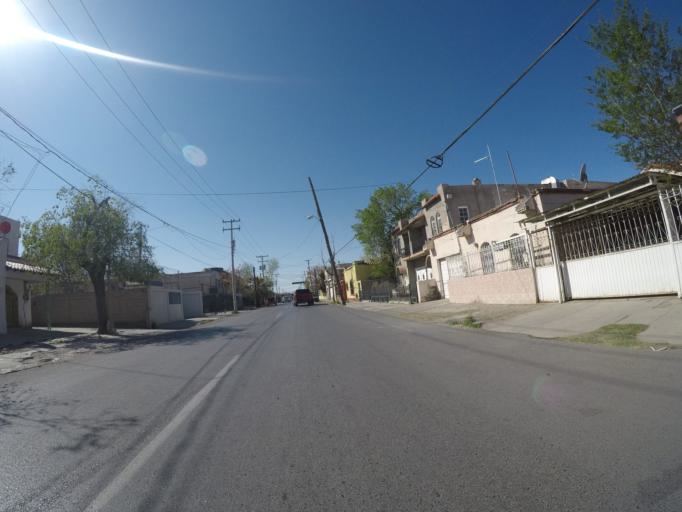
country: MX
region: Chihuahua
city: Ciudad Juarez
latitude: 31.7364
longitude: -106.4742
